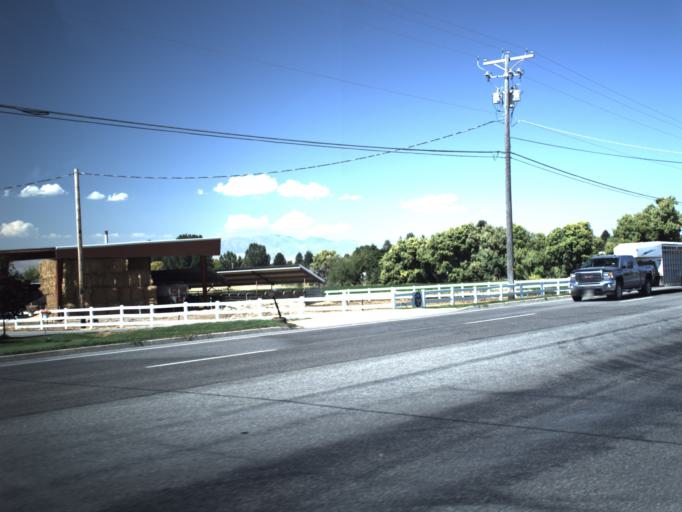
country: US
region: Utah
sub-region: Cache County
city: Richmond
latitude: 41.9163
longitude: -111.8144
